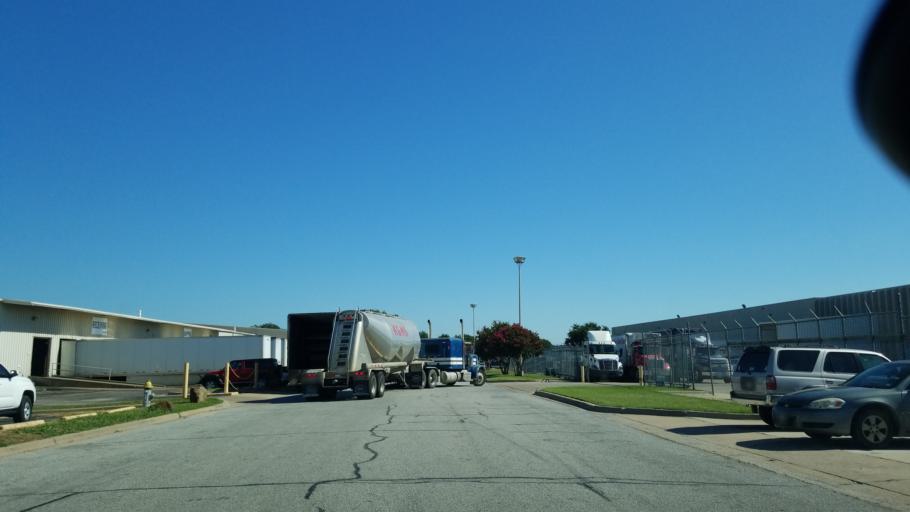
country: US
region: Texas
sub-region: Dallas County
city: Carrollton
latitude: 32.9552
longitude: -96.8841
